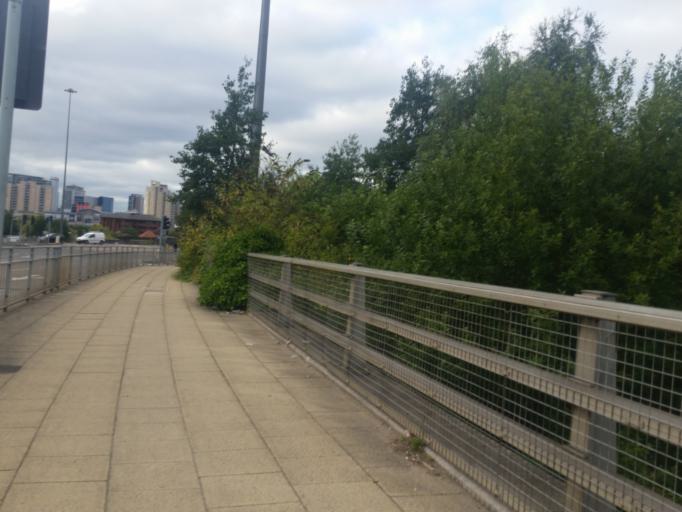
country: GB
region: England
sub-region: City and Borough of Salford
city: Salford
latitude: 53.4641
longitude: -2.2828
